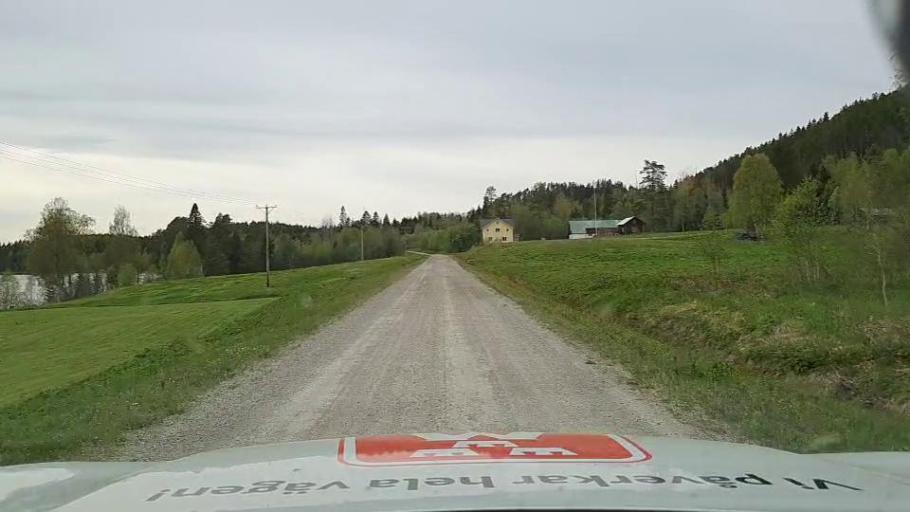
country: SE
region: Jaemtland
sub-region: Bergs Kommun
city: Hoverberg
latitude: 62.6665
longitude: 14.8191
